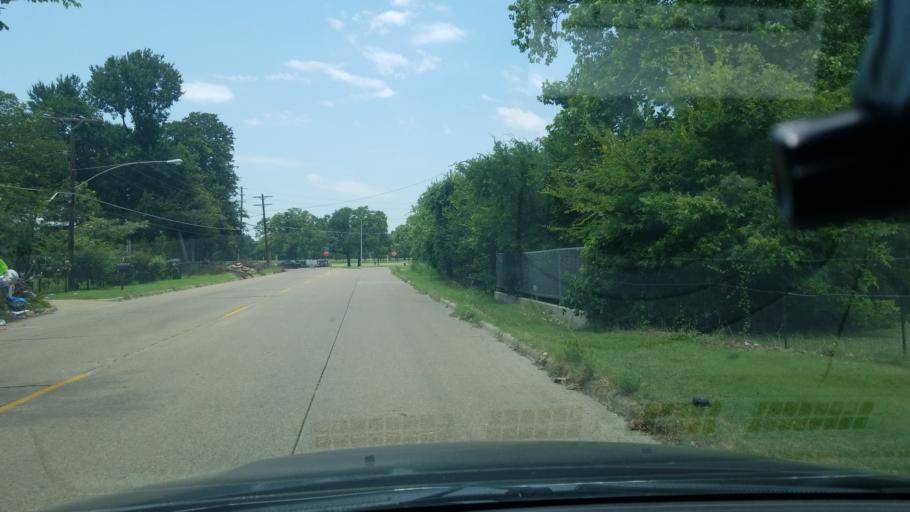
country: US
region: Texas
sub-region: Dallas County
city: Balch Springs
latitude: 32.7138
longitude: -96.6646
